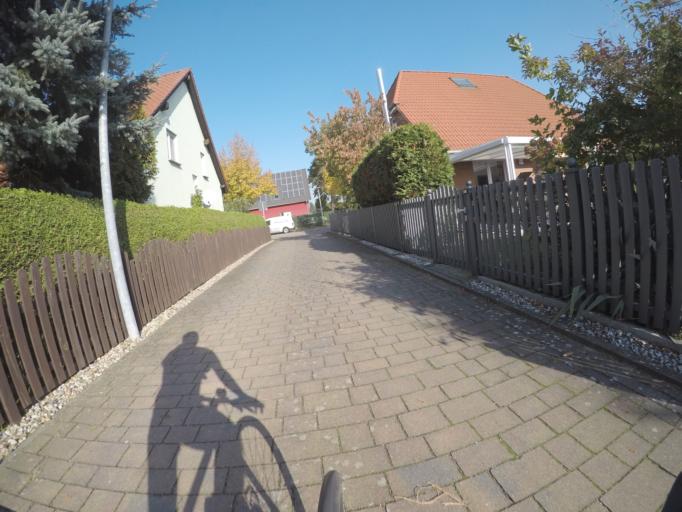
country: DE
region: Brandenburg
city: Oranienburg
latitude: 52.7333
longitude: 13.2519
